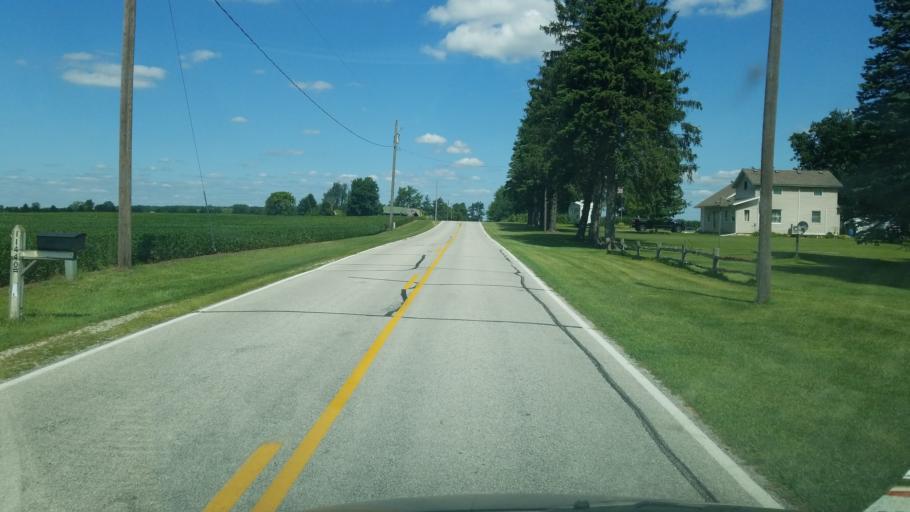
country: US
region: Ohio
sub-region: Fulton County
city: Delta
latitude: 41.6334
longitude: -84.0154
